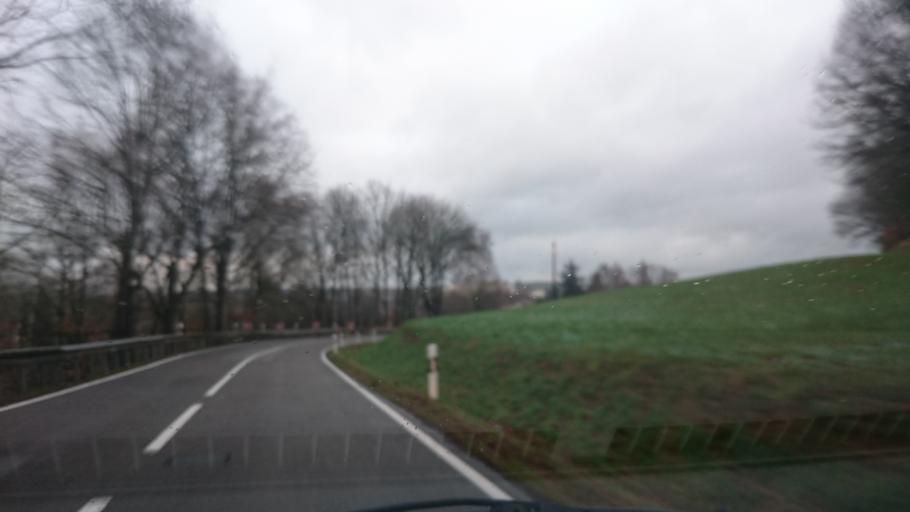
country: DE
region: Saxony
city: Sankt Egidien
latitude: 50.7770
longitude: 12.6185
